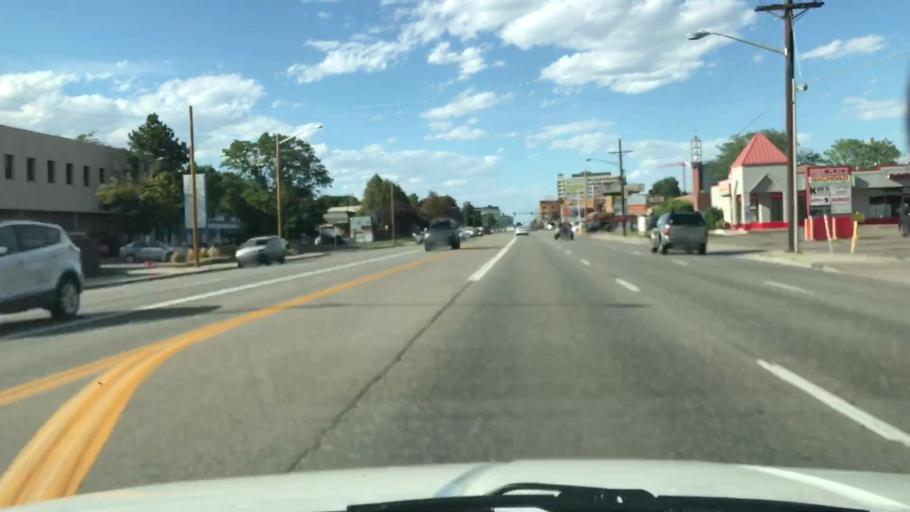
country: US
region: Colorado
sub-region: Arapahoe County
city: Glendale
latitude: 39.6722
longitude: -104.9407
